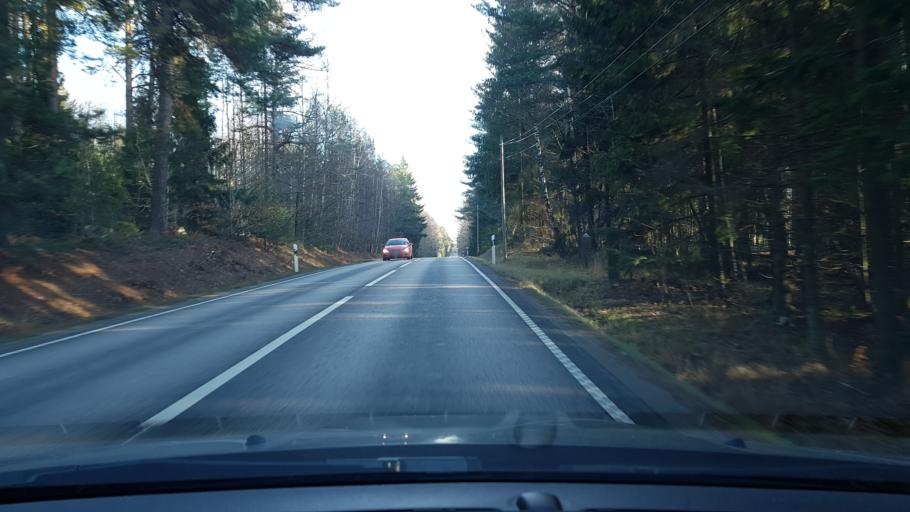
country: SE
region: Stockholm
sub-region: Norrtalje Kommun
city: Rimbo
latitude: 59.7408
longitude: 18.3123
